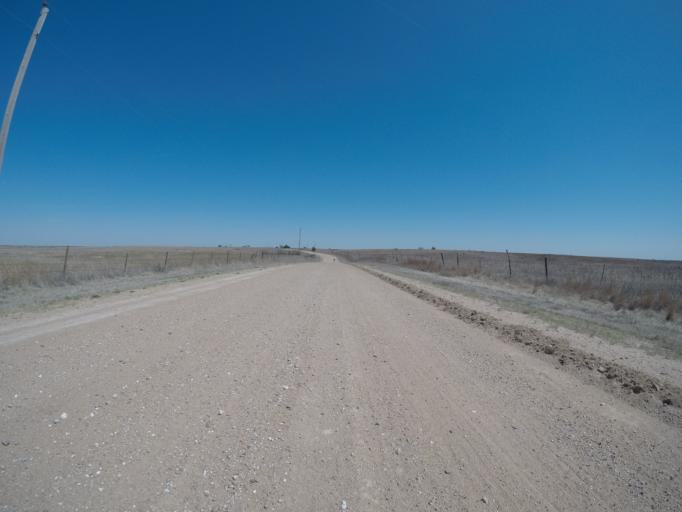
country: US
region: Kansas
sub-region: Pratt County
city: Pratt
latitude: 37.4148
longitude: -98.8391
